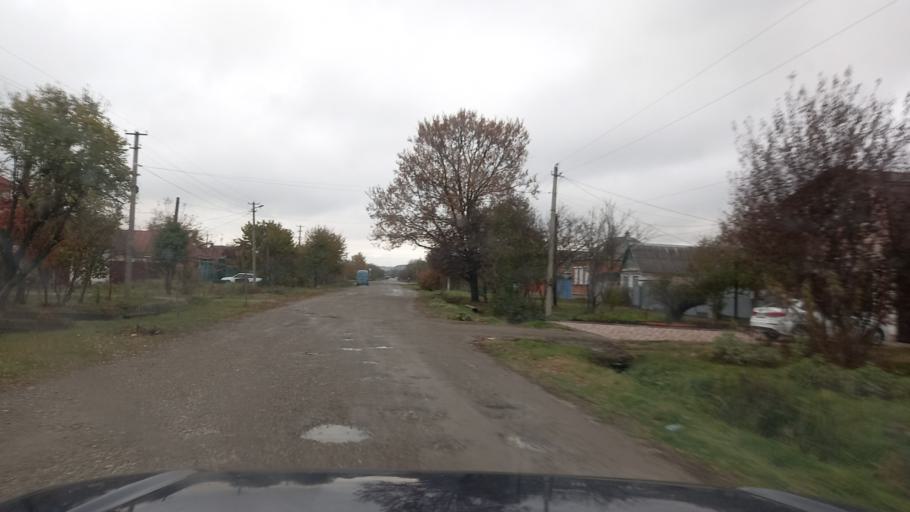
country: RU
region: Adygeya
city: Maykop
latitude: 44.6204
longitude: 40.1264
